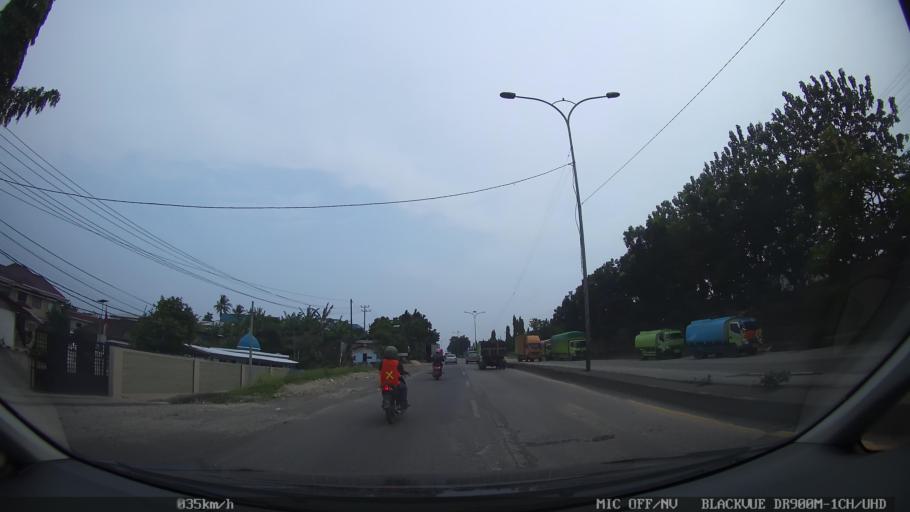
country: ID
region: Lampung
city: Bandarlampung
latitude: -5.4188
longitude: 105.2956
